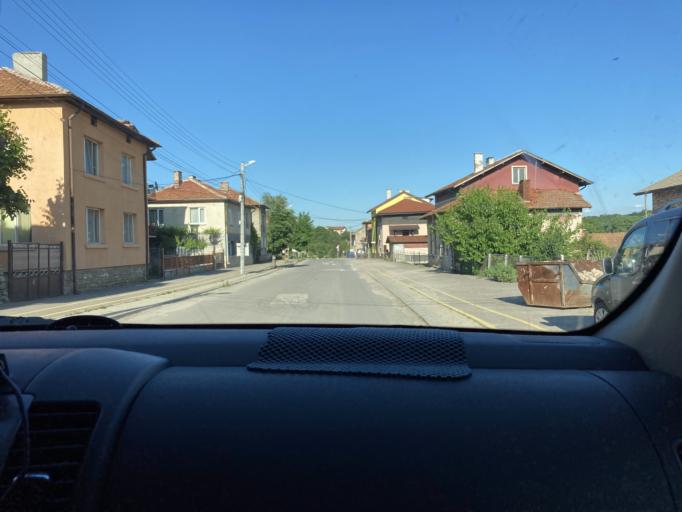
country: BG
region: Sofiya
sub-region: Obshtina Slivnitsa
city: Slivnitsa
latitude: 42.8478
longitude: 22.9866
